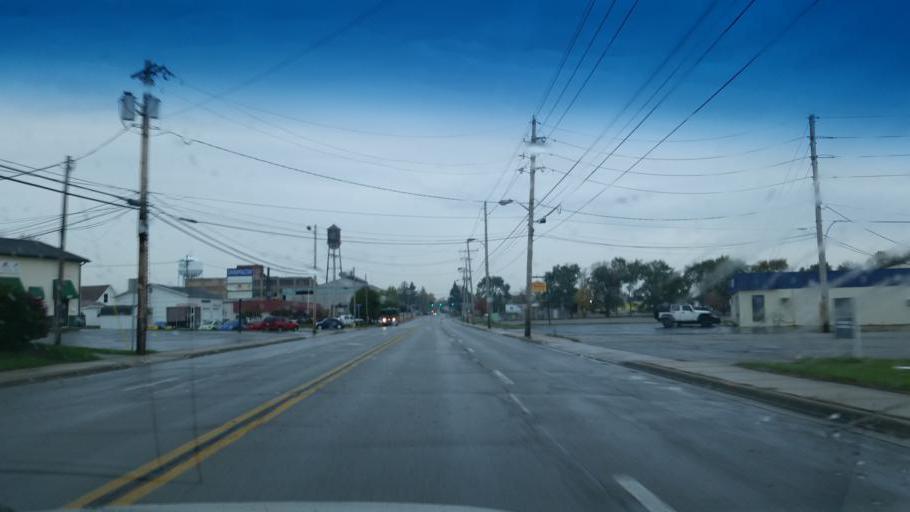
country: US
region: Indiana
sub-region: Howard County
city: Kokomo
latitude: 40.4707
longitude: -86.1263
